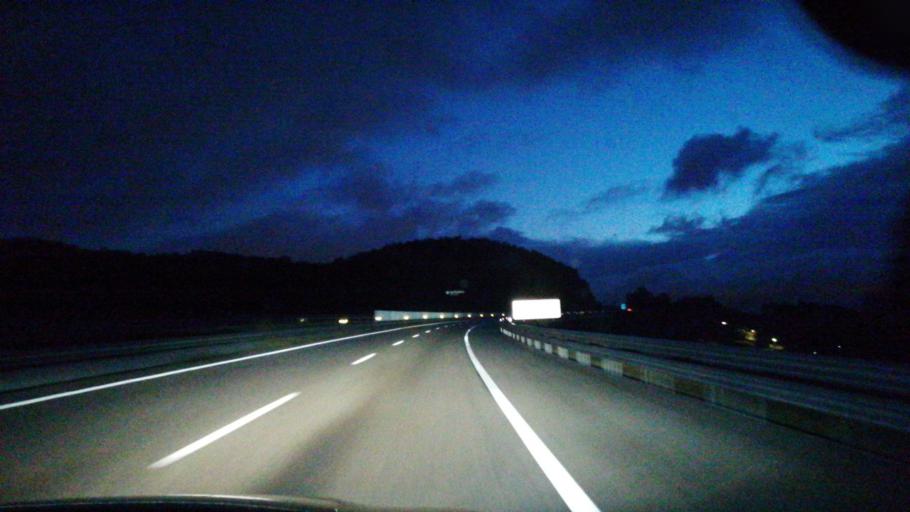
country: PT
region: Porto
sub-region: Lousada
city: Lousada
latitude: 41.3110
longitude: -8.2572
